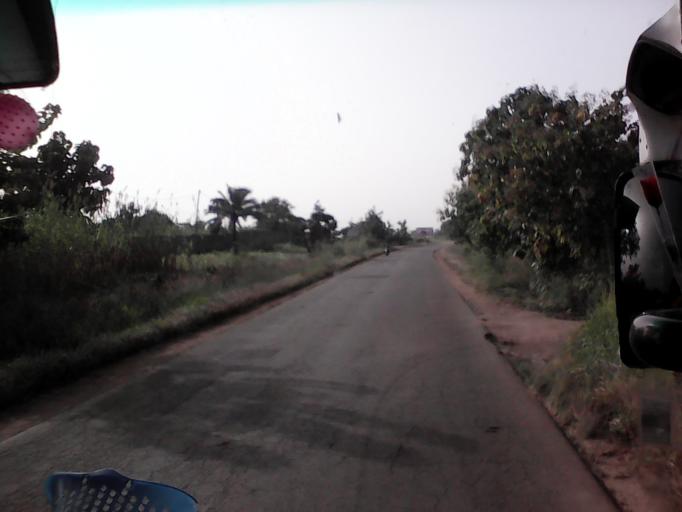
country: TG
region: Kara
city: Kara
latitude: 9.5215
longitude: 1.2082
